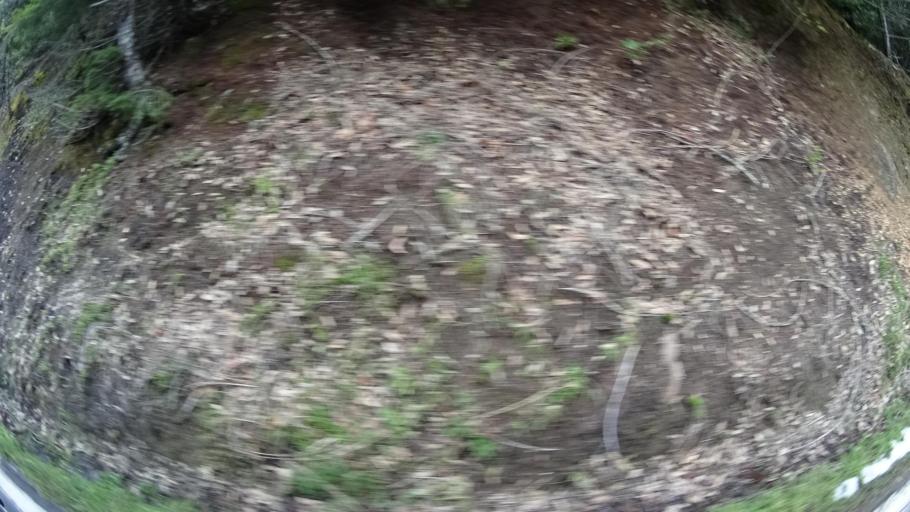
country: US
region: California
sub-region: Humboldt County
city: Willow Creek
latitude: 40.8933
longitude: -123.7689
